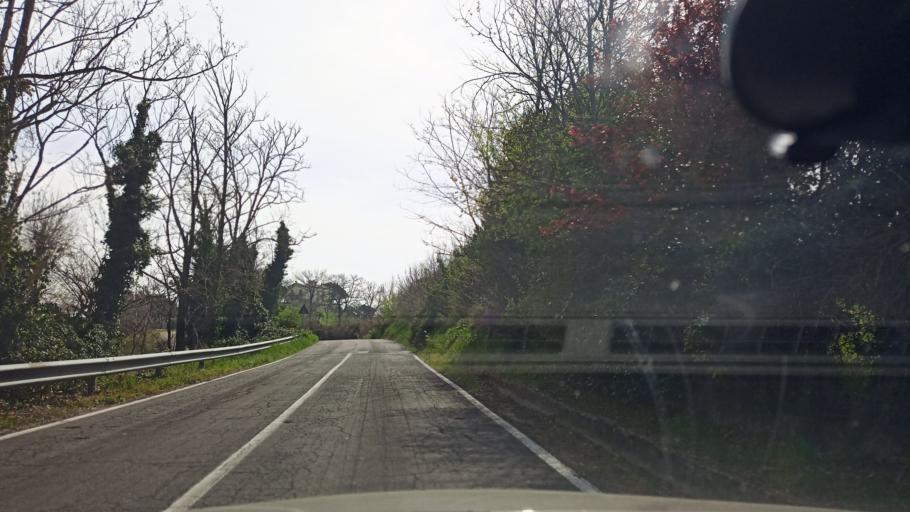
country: IT
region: Latium
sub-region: Provincia di Rieti
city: Torri in Sabina
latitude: 42.3472
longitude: 12.6500
